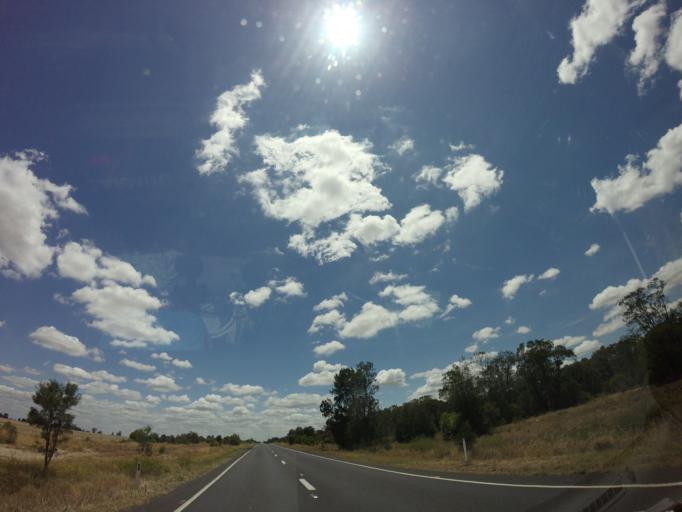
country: AU
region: New South Wales
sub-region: Moree Plains
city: Boggabilla
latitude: -28.8147
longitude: 150.2378
